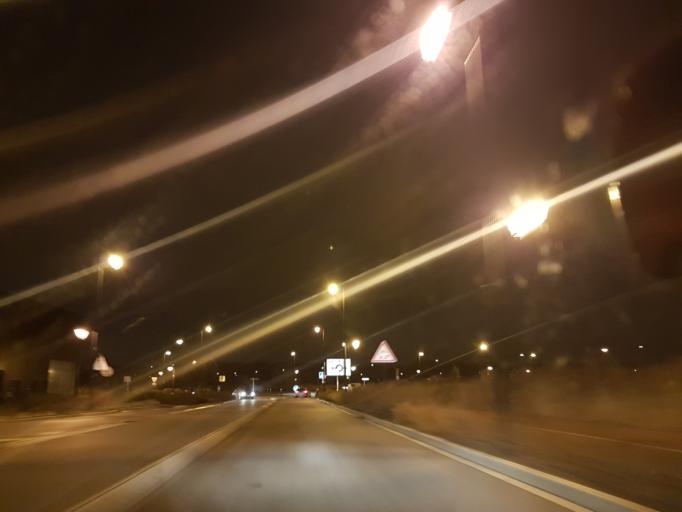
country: FR
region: Ile-de-France
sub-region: Departement des Yvelines
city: Chambourcy
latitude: 48.9108
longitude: 2.0375
